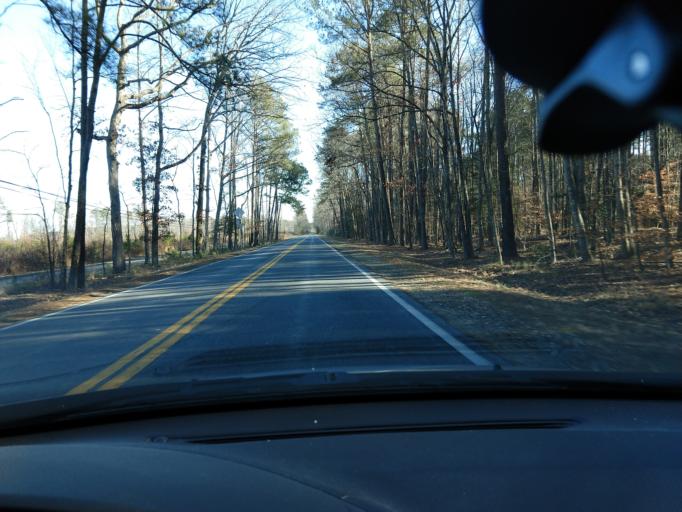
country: US
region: Virginia
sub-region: Charles City County
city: Charles City
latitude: 37.3258
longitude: -76.9829
